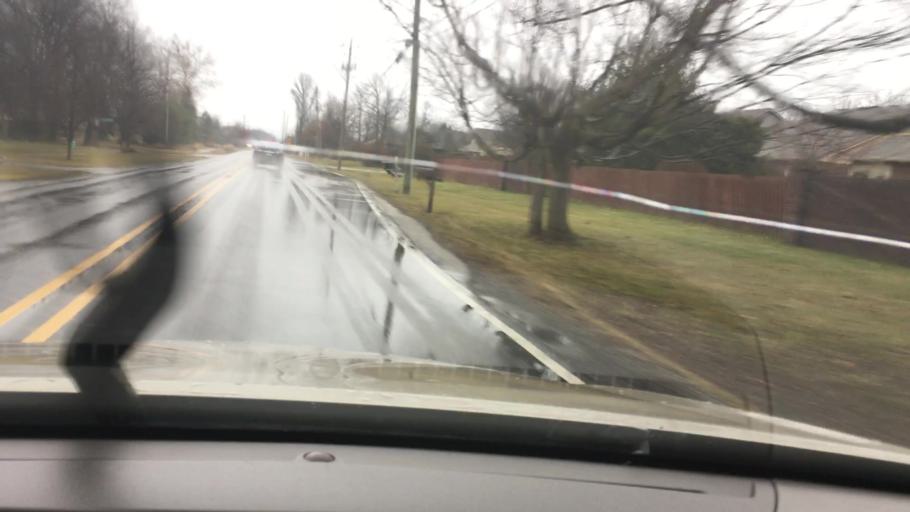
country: US
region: Indiana
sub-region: Marion County
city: Broad Ripple
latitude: 39.8833
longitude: -86.0772
